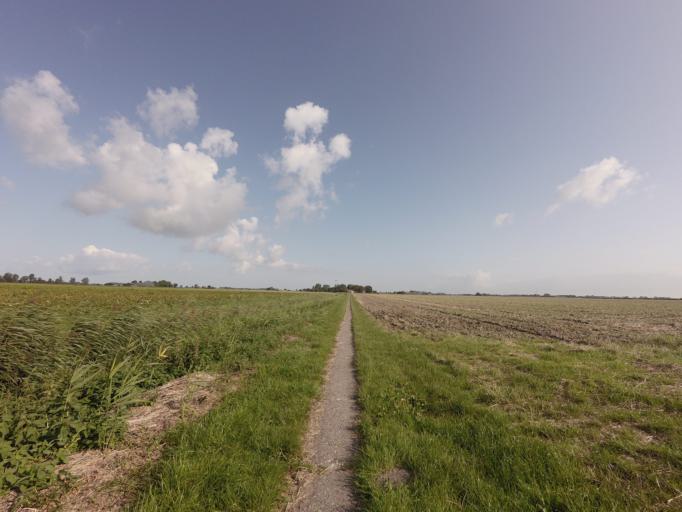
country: NL
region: Friesland
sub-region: Gemeente Franekeradeel
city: Franeker
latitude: 53.2051
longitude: 5.5646
